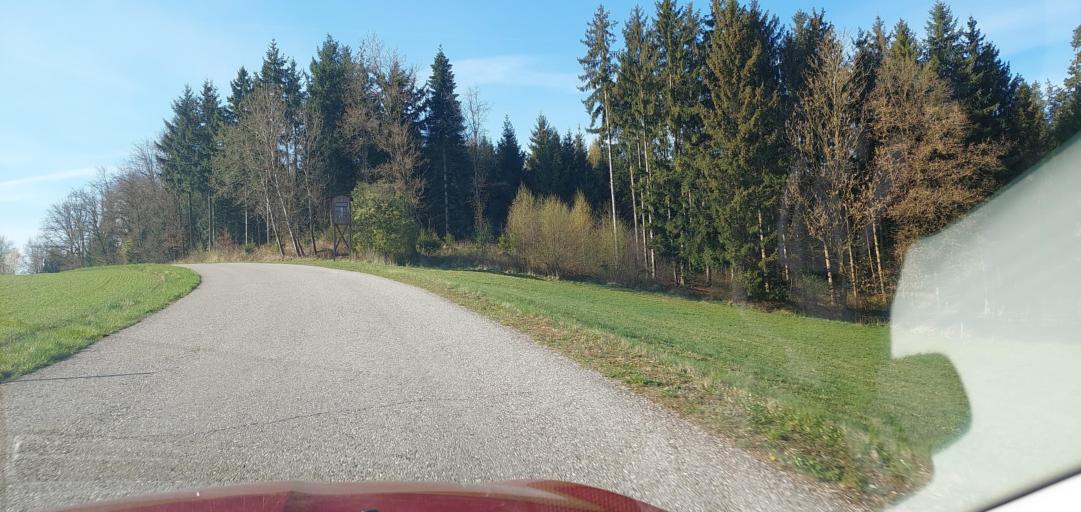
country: AT
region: Upper Austria
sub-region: Wels-Land
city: Offenhausen
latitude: 48.1766
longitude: 13.8058
